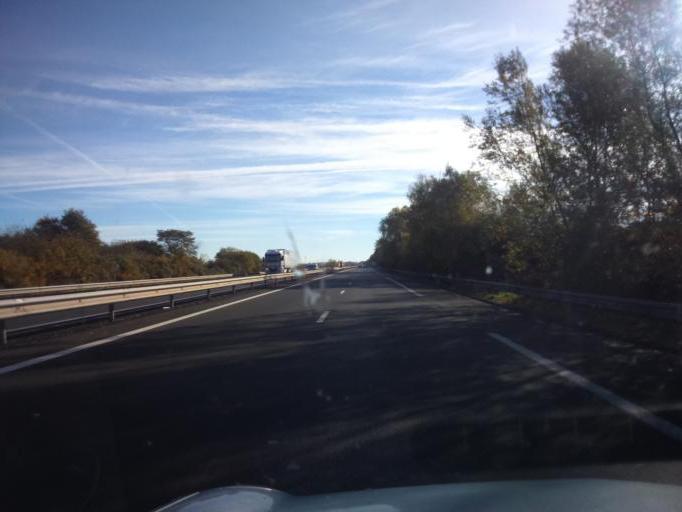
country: FR
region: Poitou-Charentes
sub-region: Departement de la Charente-Maritime
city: Breuil-Magne
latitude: 45.9608
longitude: -0.9535
